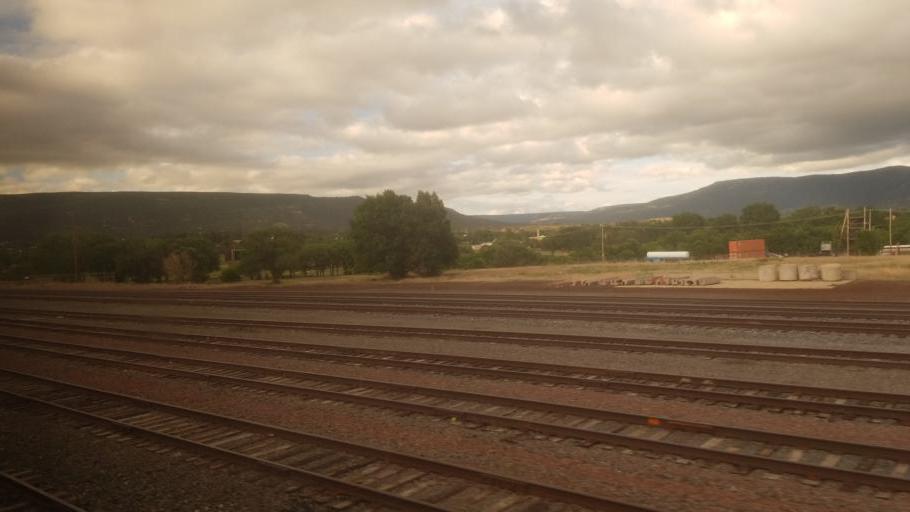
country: US
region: New Mexico
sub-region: Colfax County
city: Raton
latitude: 36.8952
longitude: -104.4388
